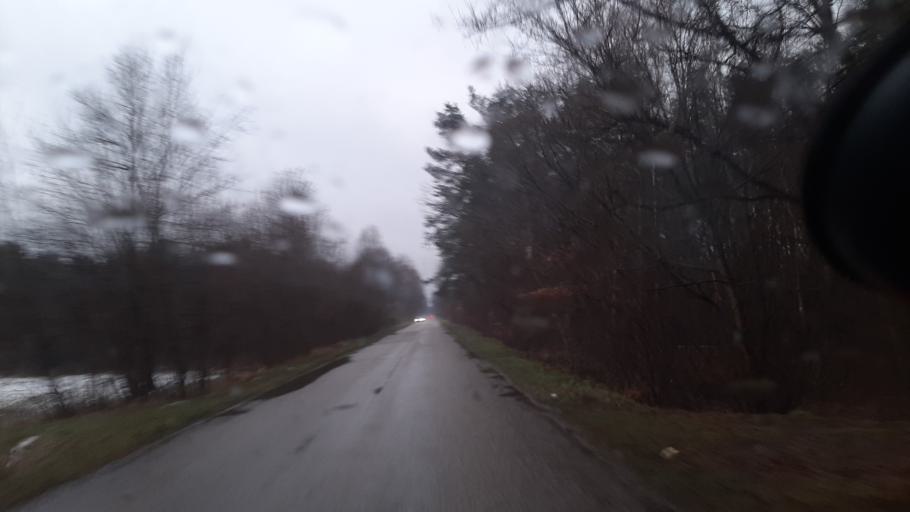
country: PL
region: Lublin Voivodeship
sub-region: Powiat lubartowski
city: Kamionka
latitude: 51.5044
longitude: 22.4886
